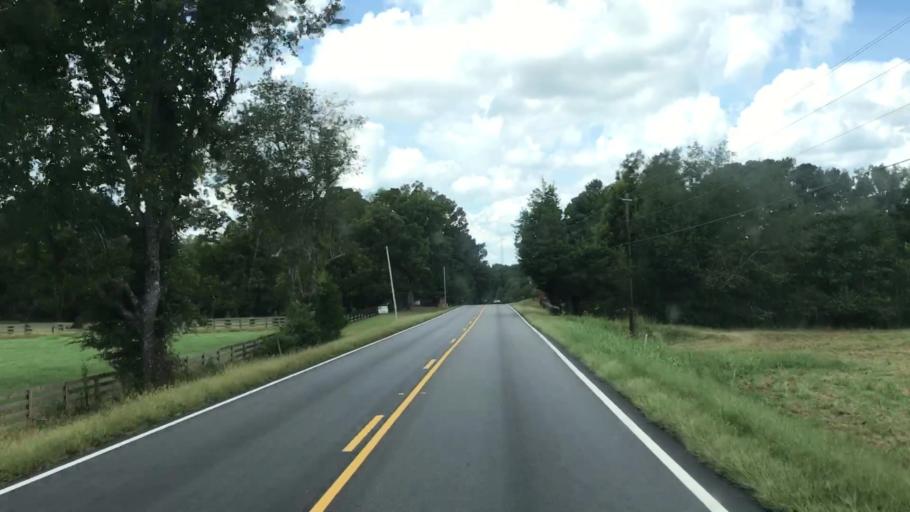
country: US
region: Georgia
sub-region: Greene County
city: Greensboro
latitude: 33.5673
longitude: -83.1591
